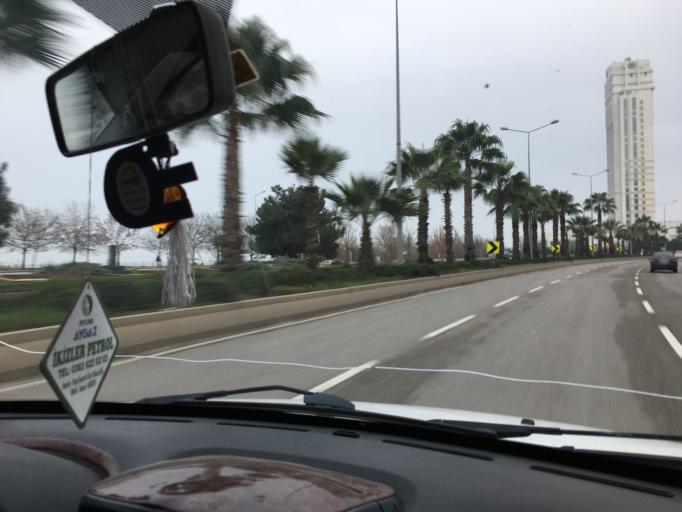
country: TR
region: Samsun
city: Samsun
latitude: 41.3161
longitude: 36.3342
